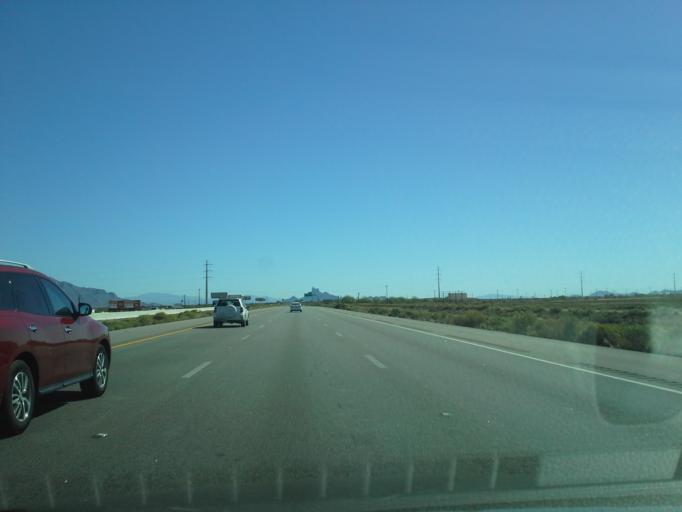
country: US
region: Arizona
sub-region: Pinal County
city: Eloy
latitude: 32.7477
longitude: -111.5721
